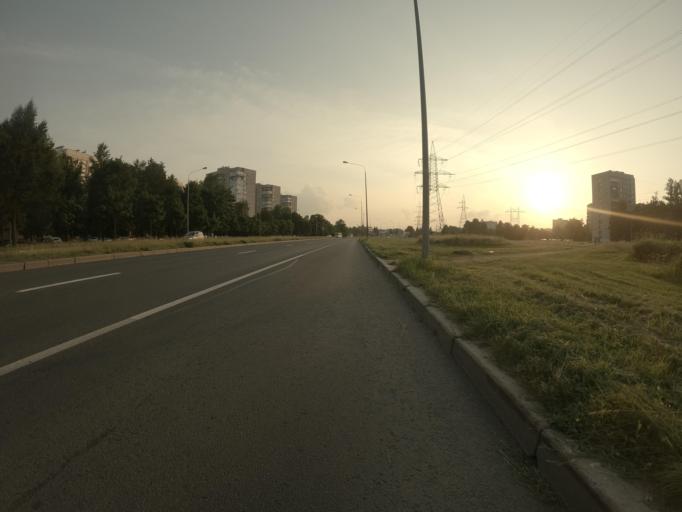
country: RU
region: Leningrad
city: Kalininskiy
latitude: 59.9747
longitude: 30.4217
